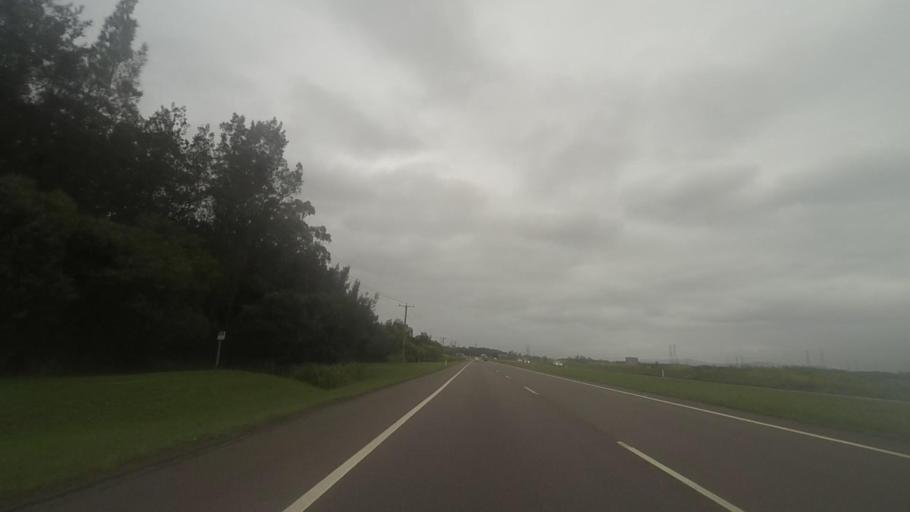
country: AU
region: New South Wales
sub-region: Port Stephens Shire
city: Raymond Terrace
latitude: -32.8023
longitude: 151.7149
